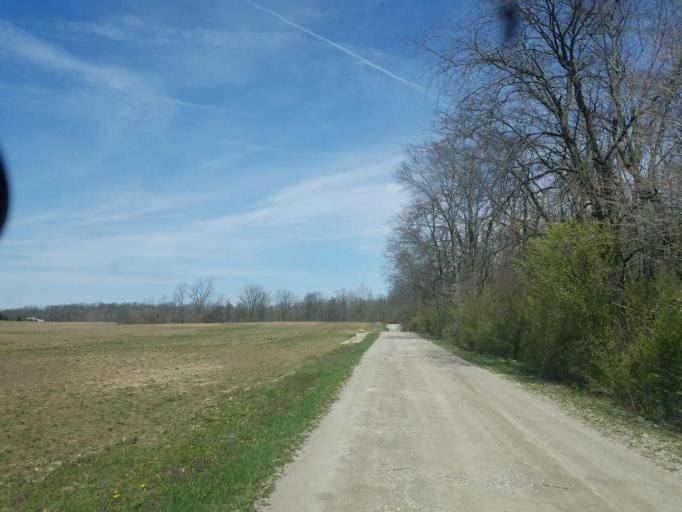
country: US
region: Ohio
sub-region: Delaware County
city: Ashley
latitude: 40.4229
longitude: -83.0588
